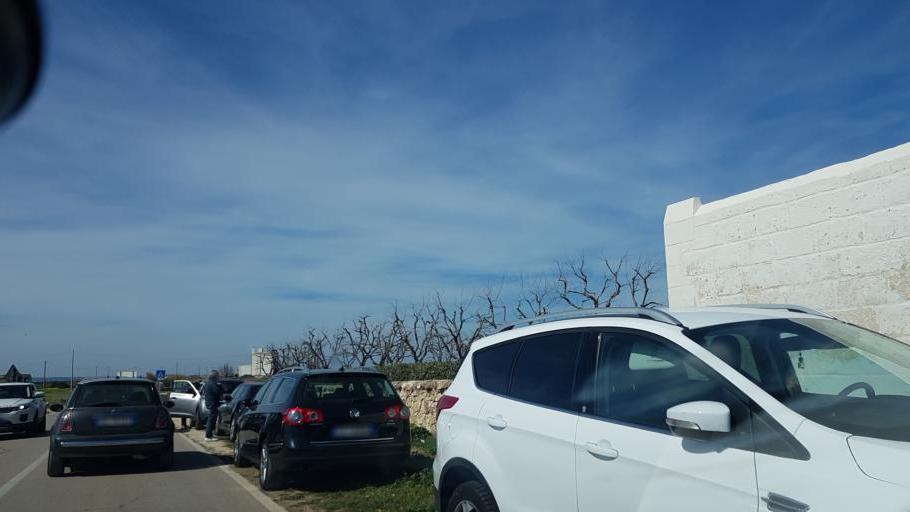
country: IT
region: Apulia
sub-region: Provincia di Brindisi
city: Pezze di Greco
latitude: 40.8537
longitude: 17.4443
